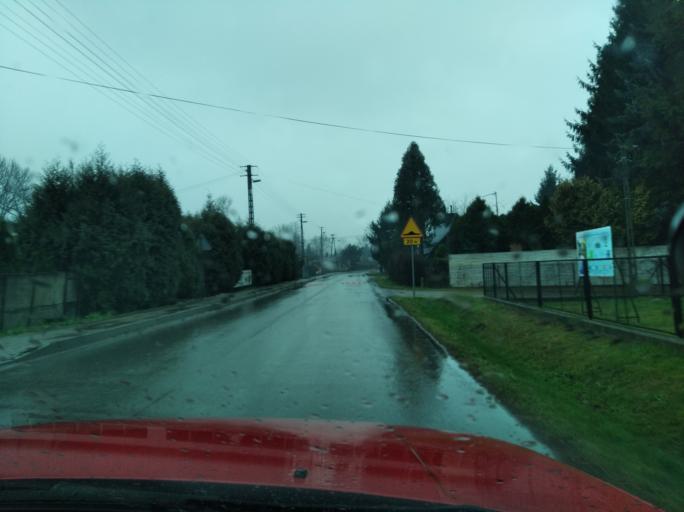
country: PL
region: Subcarpathian Voivodeship
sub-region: Powiat rzeszowski
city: Krasne
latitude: 50.0734
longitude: 22.1255
